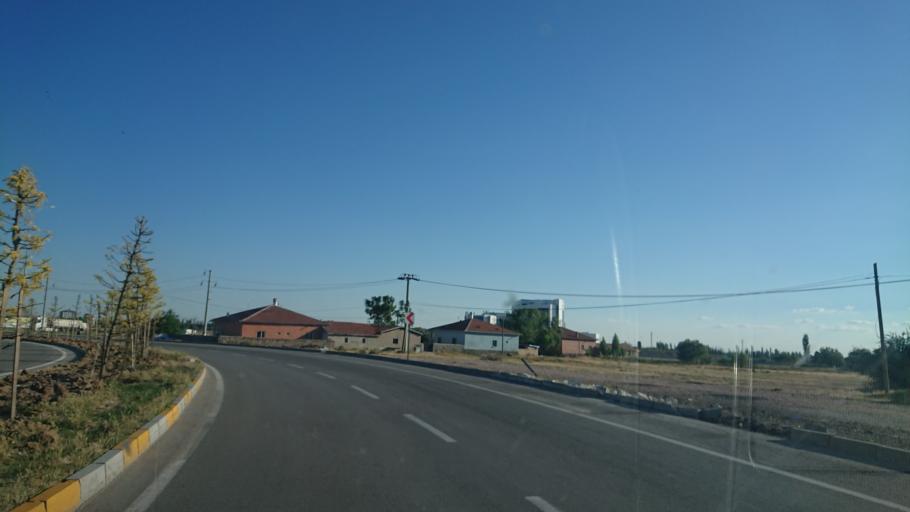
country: TR
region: Aksaray
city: Aksaray
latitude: 38.3783
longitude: 33.9877
